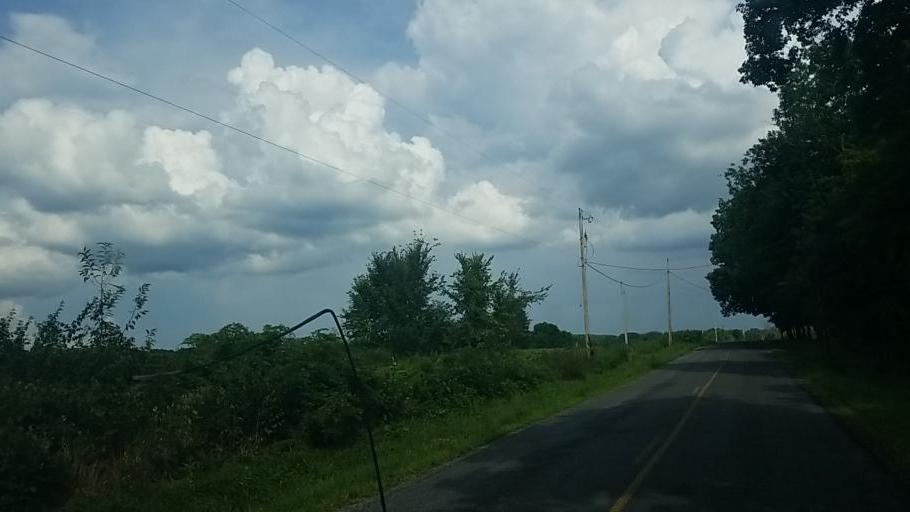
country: US
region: Ohio
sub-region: Medina County
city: Westfield Center
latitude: 41.0124
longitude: -81.9446
